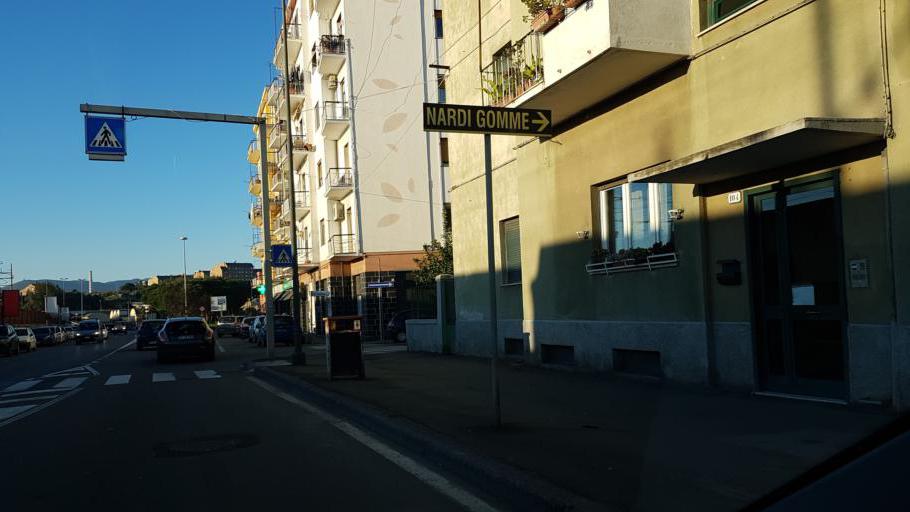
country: IT
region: Liguria
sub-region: Provincia di Savona
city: Savona
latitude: 44.2949
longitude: 8.4549
